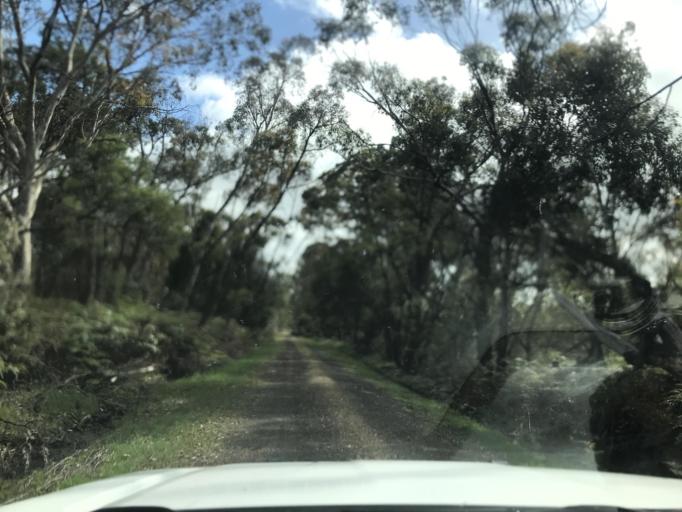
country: AU
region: South Australia
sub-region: Wattle Range
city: Penola
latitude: -37.3511
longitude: 141.3941
